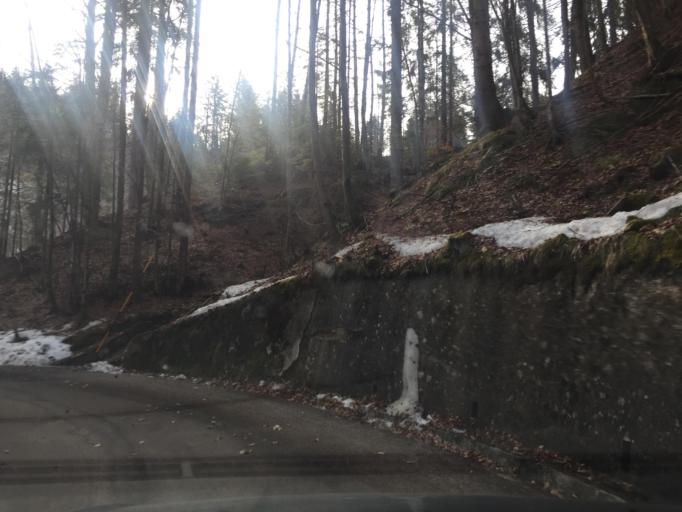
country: AT
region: Carinthia
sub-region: Politischer Bezirk Villach Land
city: Hohenthurn
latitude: 46.5079
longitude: 13.6434
